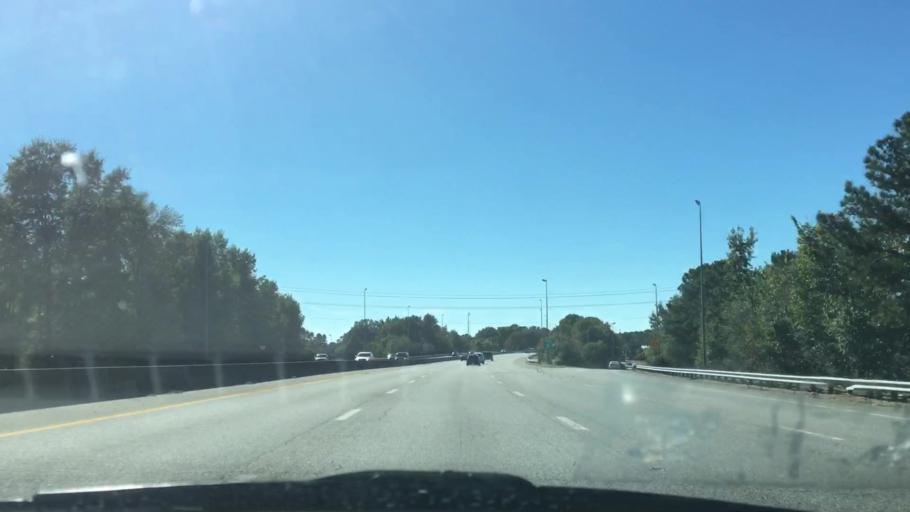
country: US
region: Virginia
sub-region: City of Portsmouth
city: Portsmouth Heights
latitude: 36.8100
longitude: -76.3529
